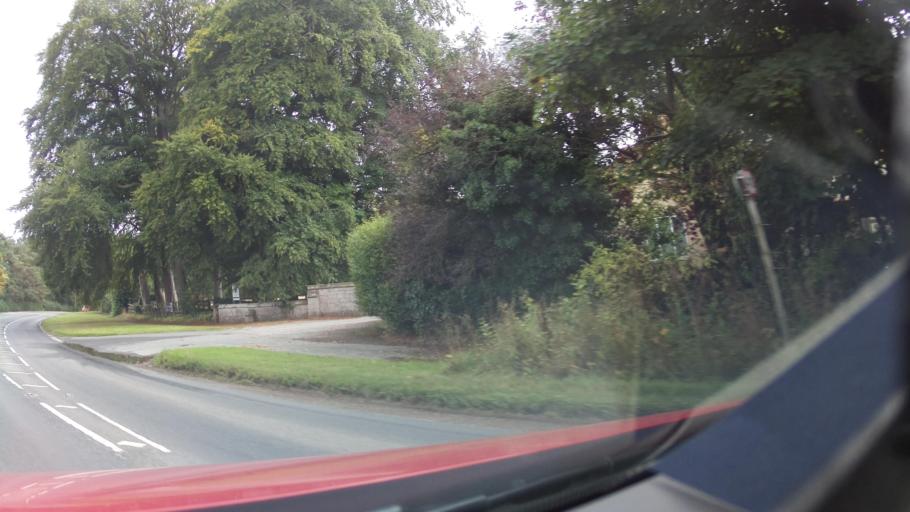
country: GB
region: England
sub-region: North Yorkshire
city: Ripon
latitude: 54.1527
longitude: -1.5331
